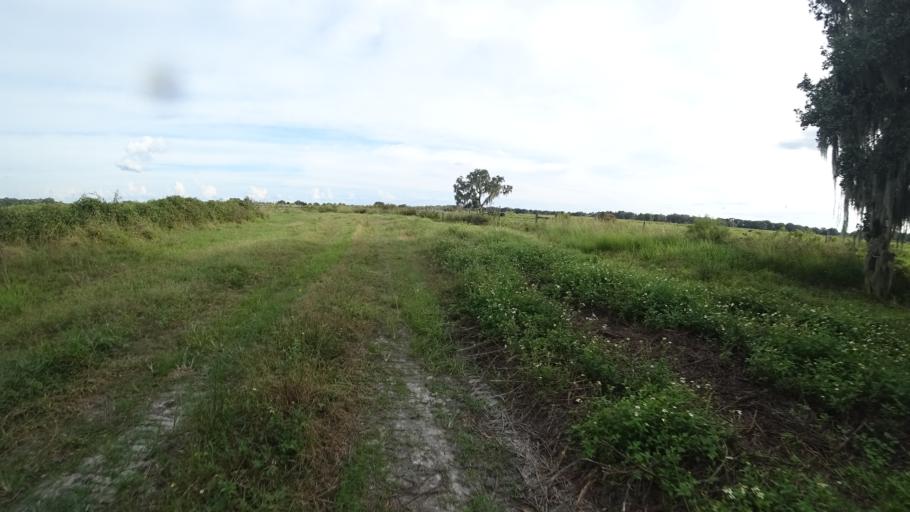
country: US
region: Florida
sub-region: Hillsborough County
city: Wimauma
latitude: 27.5519
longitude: -82.0926
